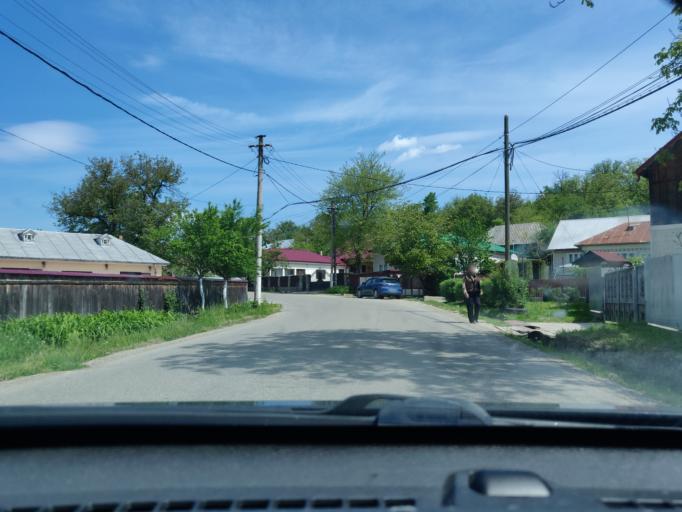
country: RO
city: Vizantea-Manastireasca
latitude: 45.9716
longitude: 26.8128
